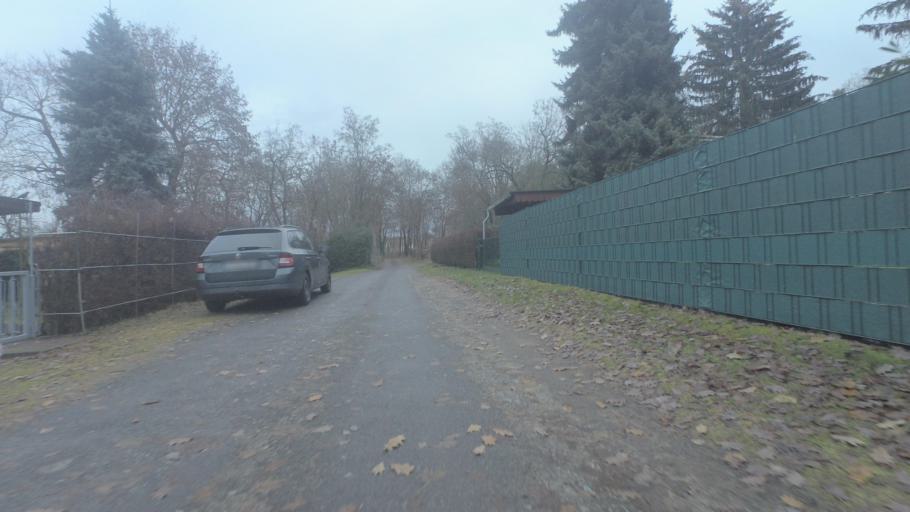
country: DE
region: Brandenburg
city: Ludwigsfelde
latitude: 52.2818
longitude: 13.2083
